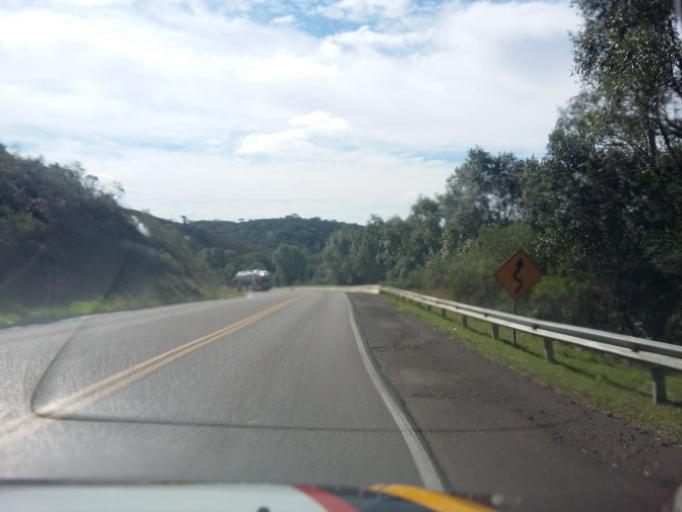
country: BR
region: Rio Grande do Sul
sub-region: Vacaria
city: Vacaria
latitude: -28.5926
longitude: -51.0297
